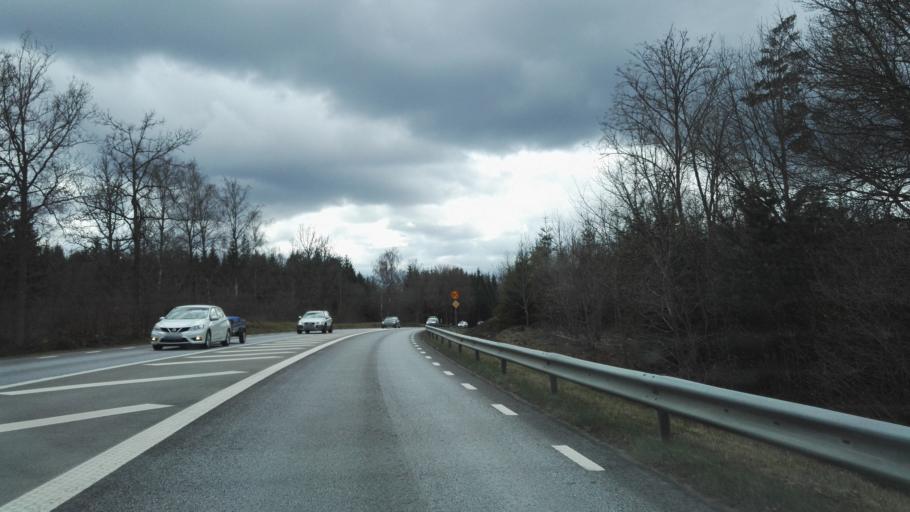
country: SE
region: Kronoberg
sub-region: Vaxjo Kommun
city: Gemla
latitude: 56.8176
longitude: 14.6861
